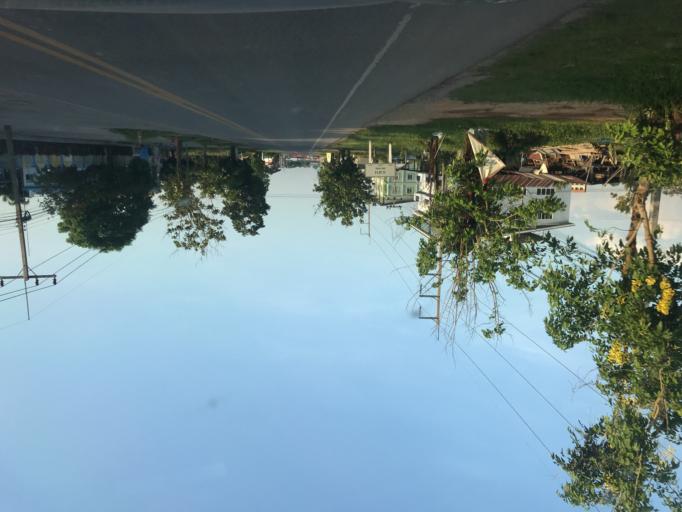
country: TH
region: Phayao
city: Chiang Kham
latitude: 19.5233
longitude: 100.2952
